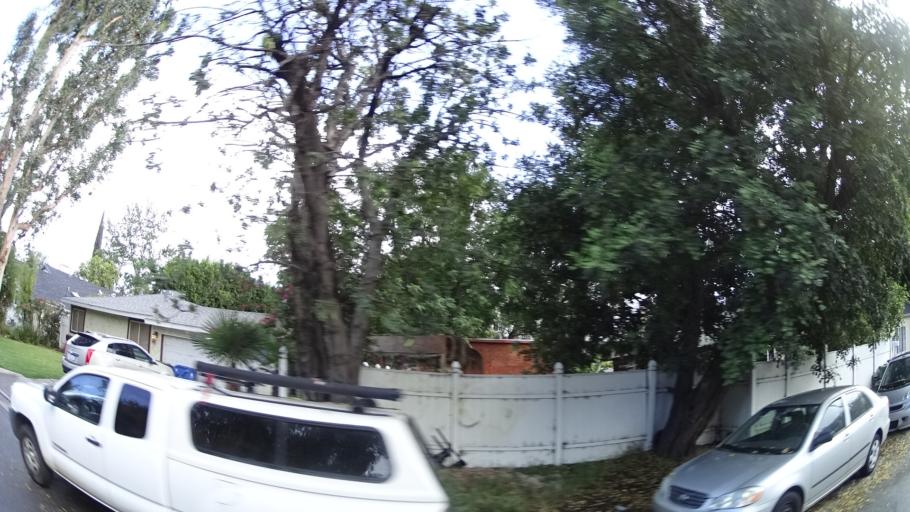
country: US
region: California
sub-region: Los Angeles County
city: Sherman Oaks
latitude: 34.1548
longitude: -118.4379
